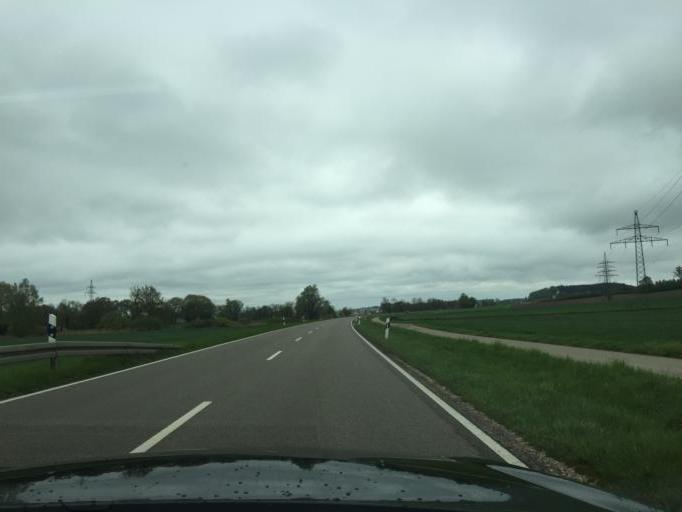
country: DE
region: Bavaria
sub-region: Swabia
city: Wertingen
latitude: 48.5683
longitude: 10.7040
